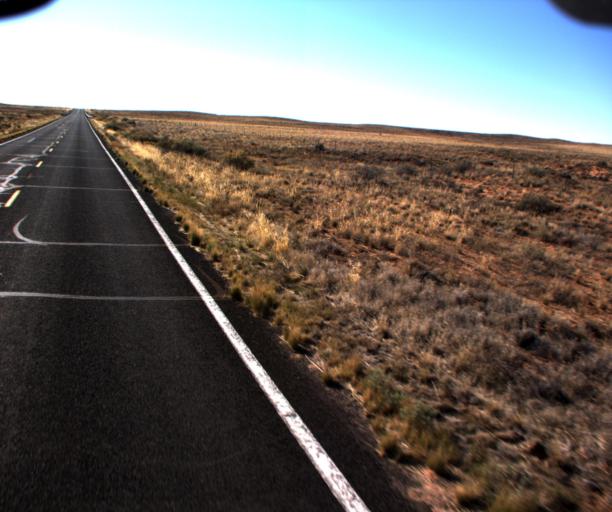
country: US
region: Arizona
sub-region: Navajo County
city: First Mesa
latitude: 35.6486
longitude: -110.4886
